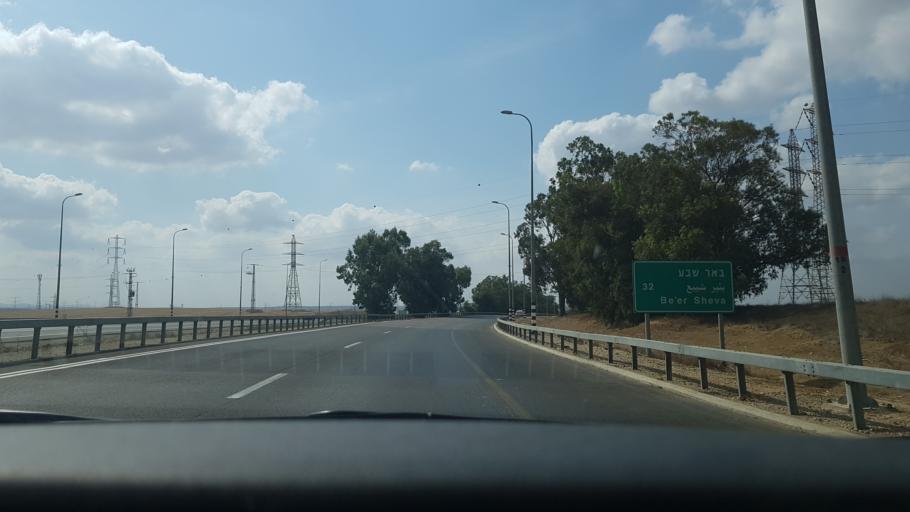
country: IL
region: Southern District
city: Qiryat Gat
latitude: 31.5004
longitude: 34.7833
